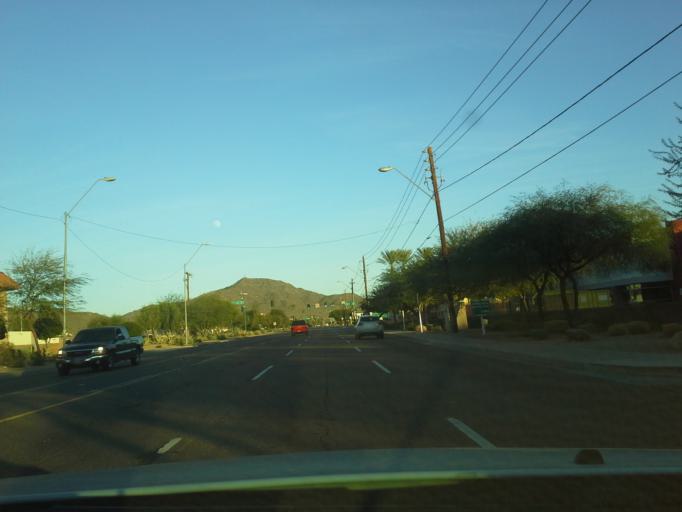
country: US
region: Arizona
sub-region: Maricopa County
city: Glendale
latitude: 33.5820
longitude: -112.1055
